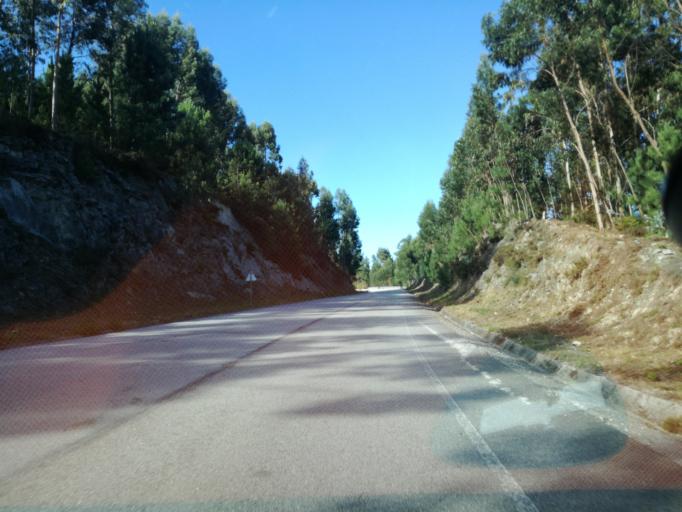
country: PT
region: Porto
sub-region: Pacos de Ferreira
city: Seroa
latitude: 41.2845
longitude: -8.4245
